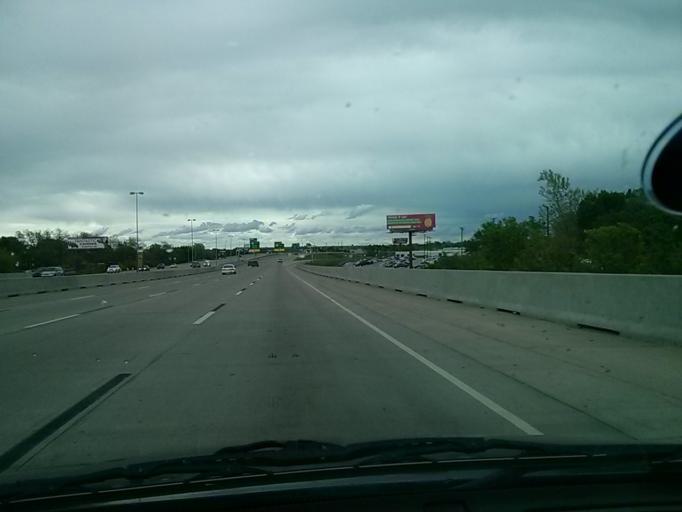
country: US
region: Oklahoma
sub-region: Tulsa County
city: Owasso
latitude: 36.1629
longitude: -95.8760
